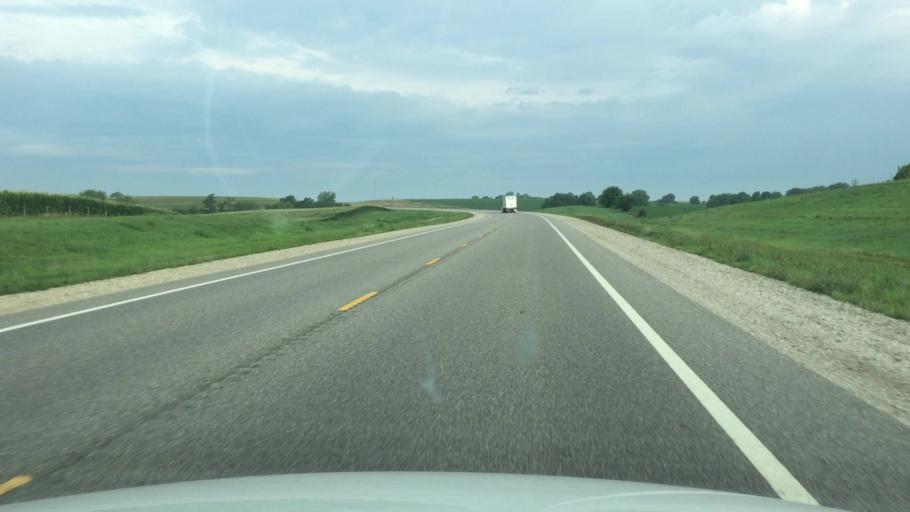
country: US
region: Kansas
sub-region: Doniphan County
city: Highland
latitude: 39.8323
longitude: -95.2316
